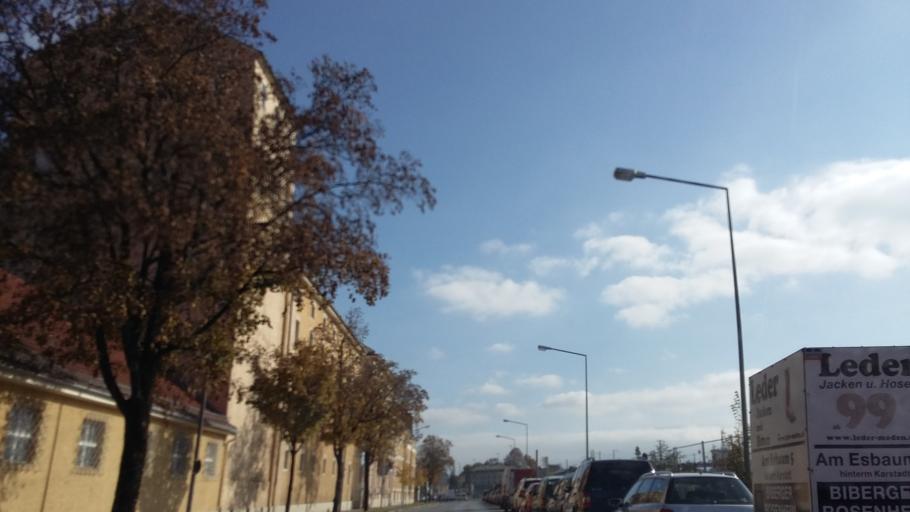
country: DE
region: Bavaria
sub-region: Upper Bavaria
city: Rosenheim
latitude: 47.8529
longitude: 12.1139
